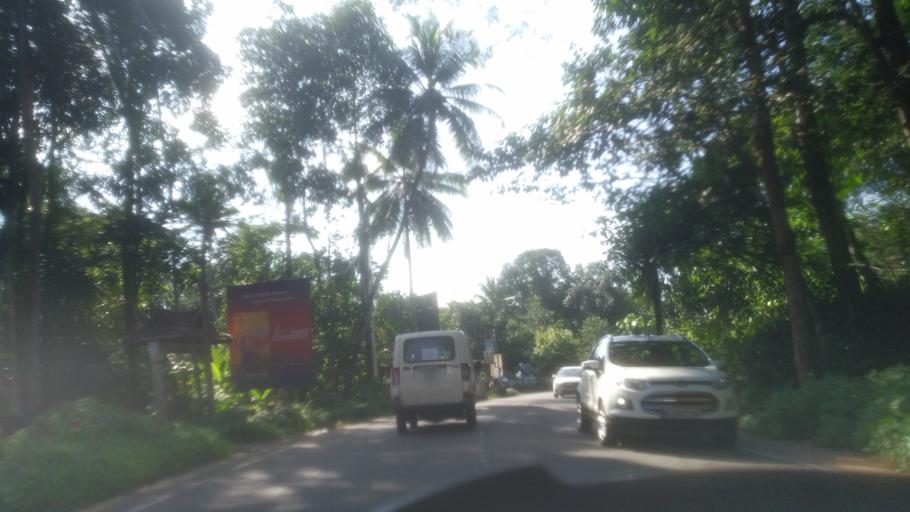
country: IN
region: Kerala
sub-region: Ernakulam
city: Muvattupuzha
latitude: 9.9795
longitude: 76.5484
